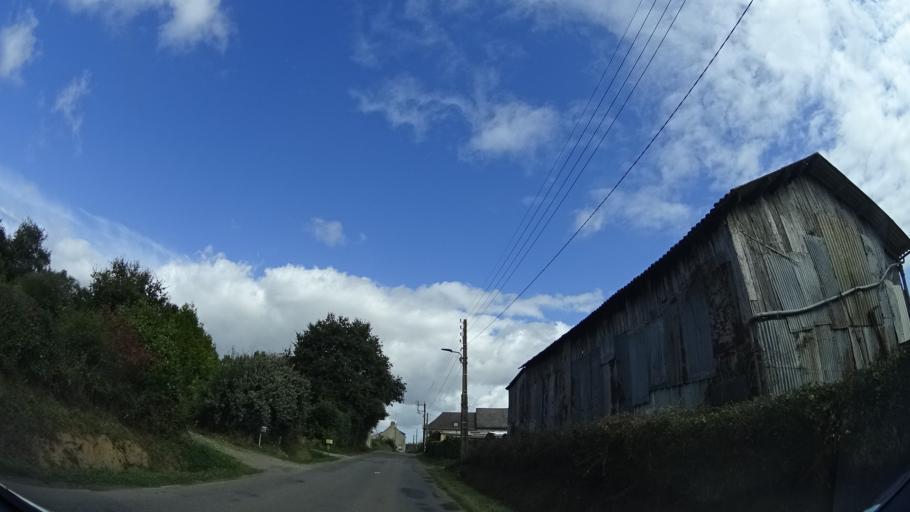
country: FR
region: Brittany
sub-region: Departement d'Ille-et-Vilaine
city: Montreuil-sur-Ille
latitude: 48.3154
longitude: -1.6791
